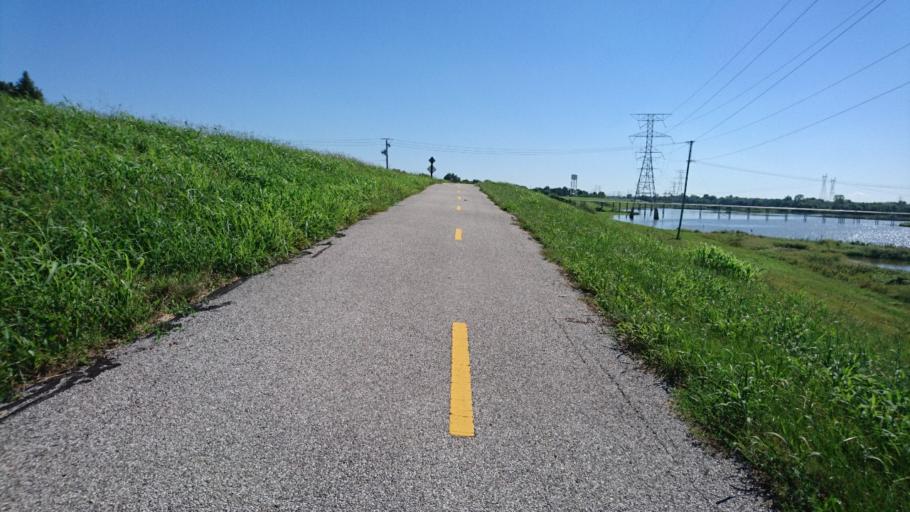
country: US
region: Illinois
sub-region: Madison County
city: Hartford
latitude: 38.8403
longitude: -90.0982
